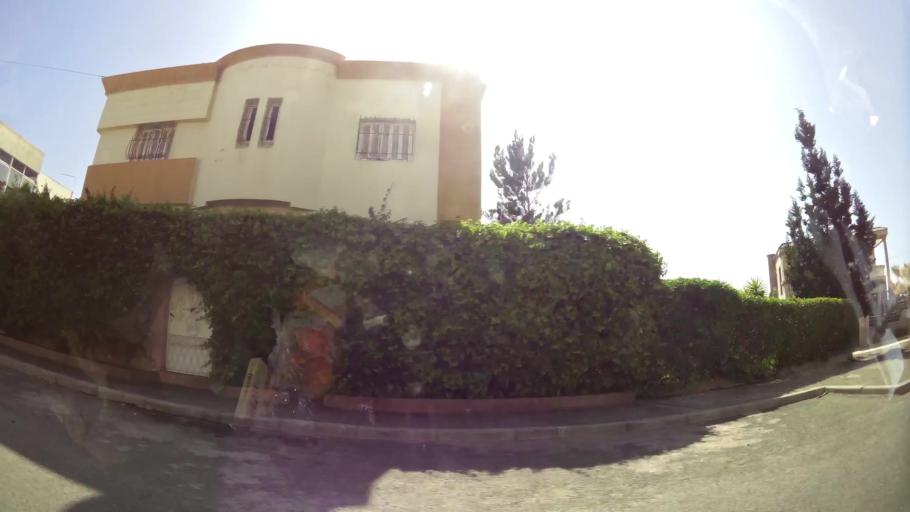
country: MA
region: Souss-Massa-Draa
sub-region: Agadir-Ida-ou-Tnan
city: Agadir
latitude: 30.3930
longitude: -9.5921
